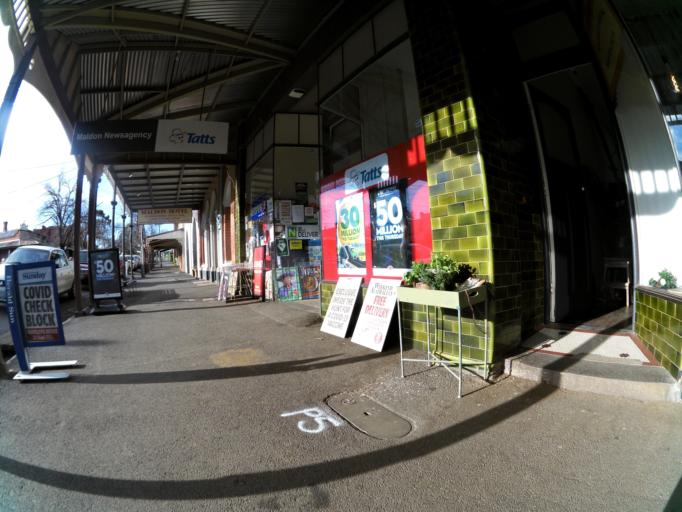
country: AU
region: Victoria
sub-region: Mount Alexander
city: Castlemaine
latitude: -36.9972
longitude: 144.0692
